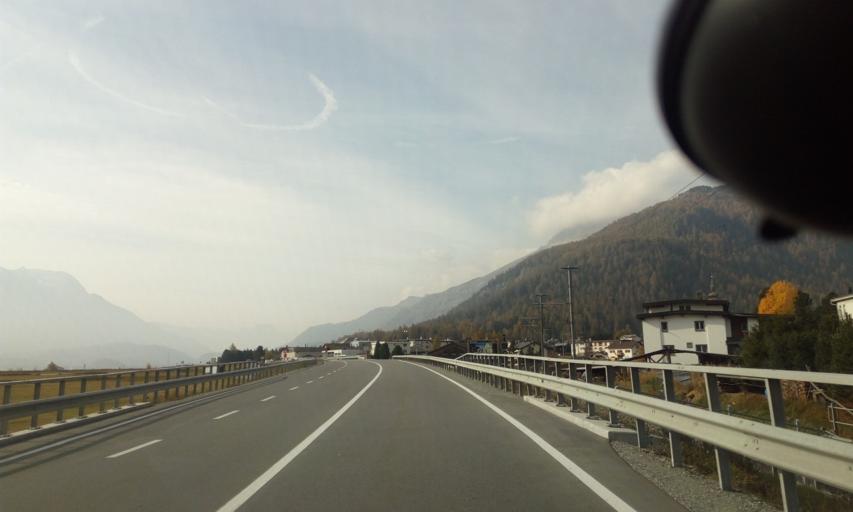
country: CH
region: Grisons
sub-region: Maloja District
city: Samedan
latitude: 46.5535
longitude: 9.8940
